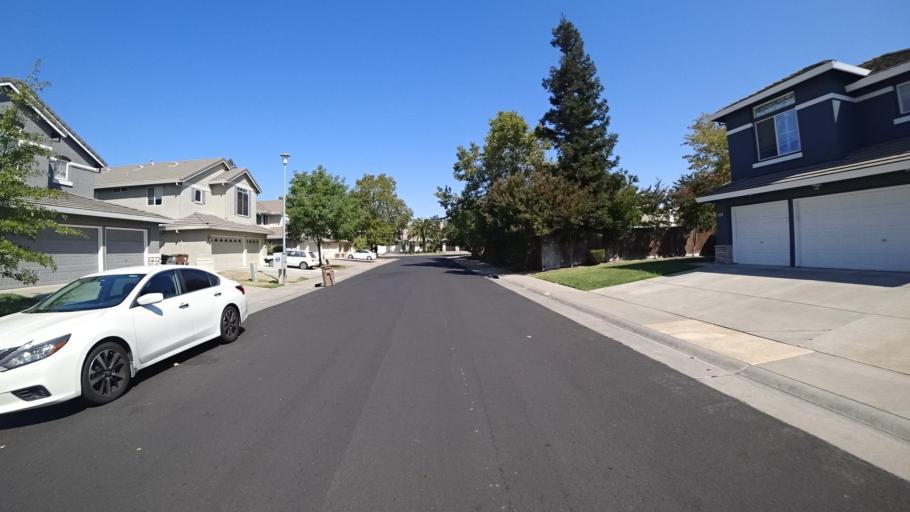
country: US
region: California
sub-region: Sacramento County
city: Elk Grove
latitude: 38.4479
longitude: -121.3869
